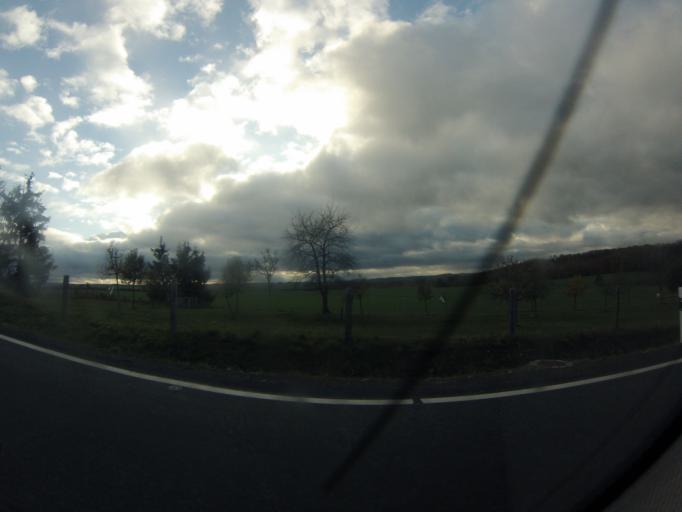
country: DE
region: Thuringia
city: Nobdenitz
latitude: 50.8681
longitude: 12.2869
